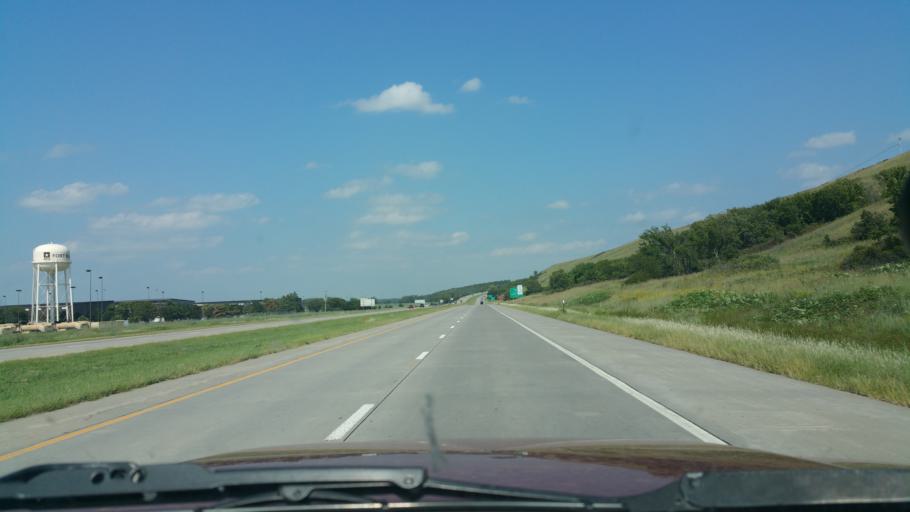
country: US
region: Kansas
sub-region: Geary County
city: Grandview Plaza
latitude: 39.0447
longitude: -96.7609
